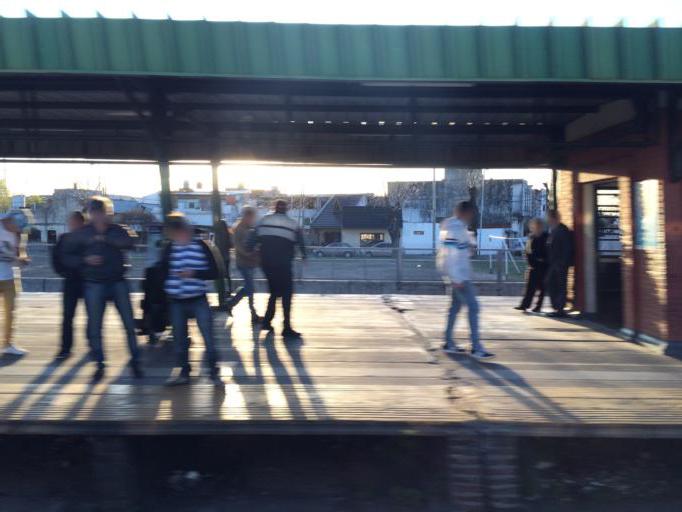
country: AR
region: Buenos Aires
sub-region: Partido de Lanus
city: Lanus
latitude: -34.6861
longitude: -58.3827
